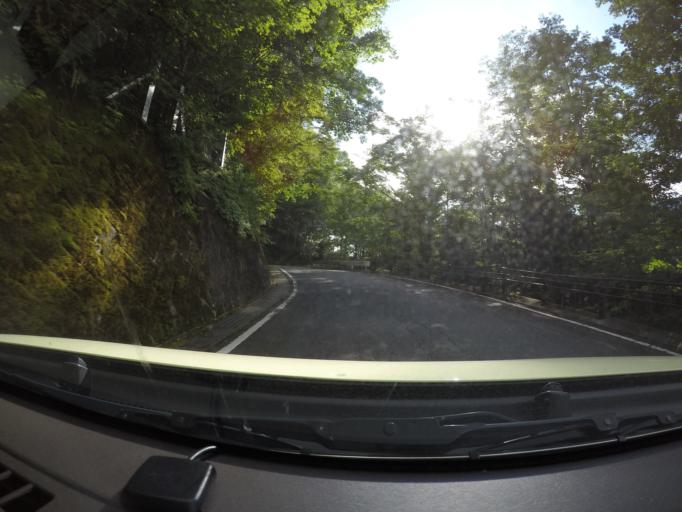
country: JP
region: Tochigi
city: Nikko
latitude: 36.8235
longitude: 139.3480
